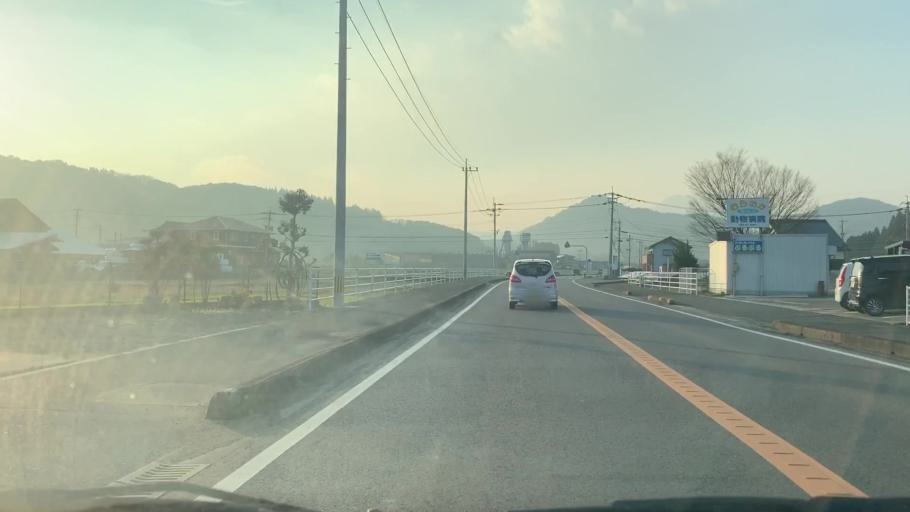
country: JP
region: Saga Prefecture
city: Takeocho-takeo
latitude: 33.2722
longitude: 130.1240
